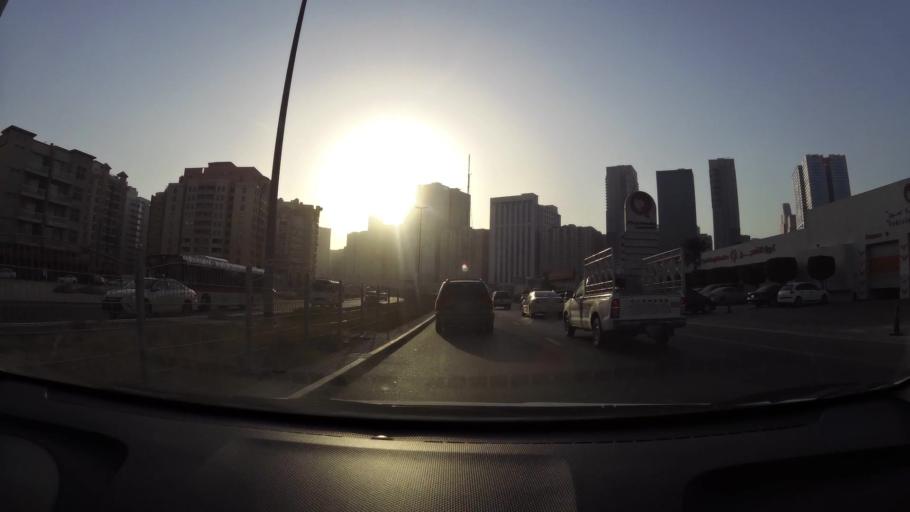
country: AE
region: Ash Shariqah
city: Sharjah
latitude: 25.2974
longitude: 55.3856
